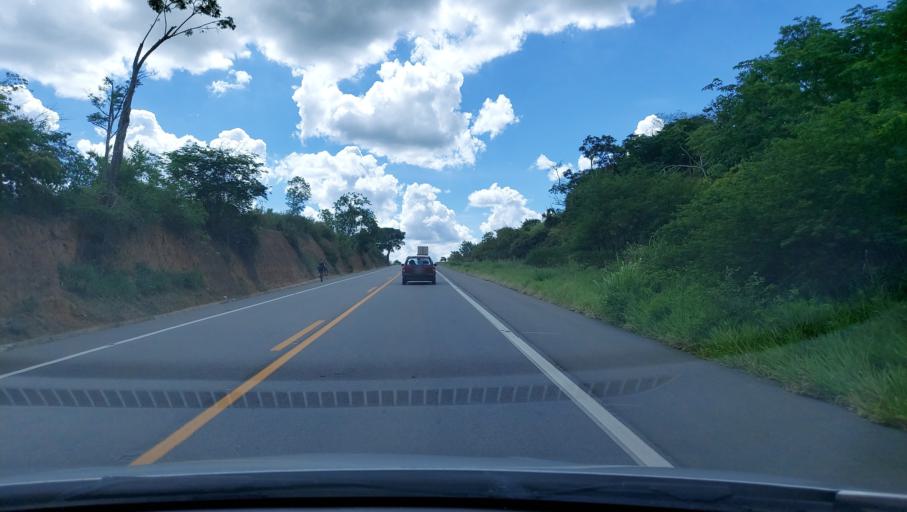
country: BR
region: Bahia
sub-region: Ruy Barbosa
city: Terra Nova
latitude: -12.4497
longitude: -40.6490
